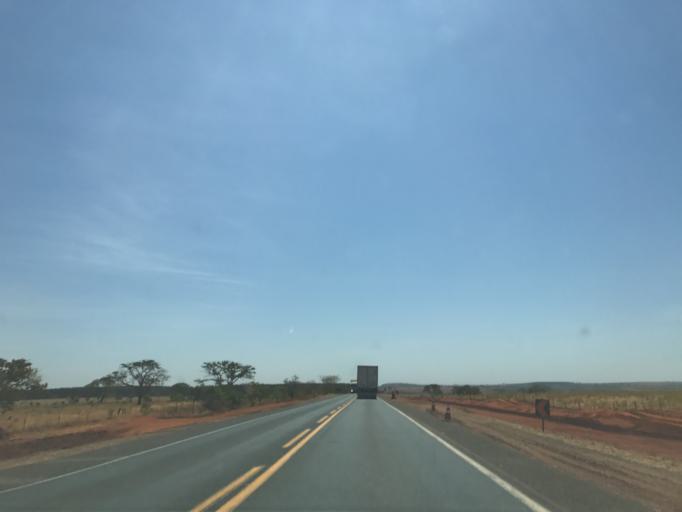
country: BR
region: Minas Gerais
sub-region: Prata
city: Prata
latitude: -19.4620
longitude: -48.8777
